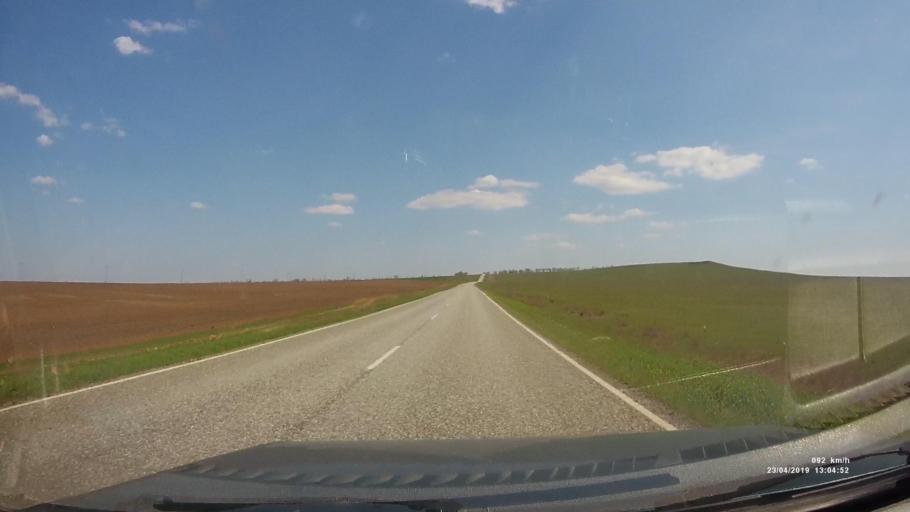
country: RU
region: Kalmykiya
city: Yashalta
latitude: 46.5930
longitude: 42.7121
